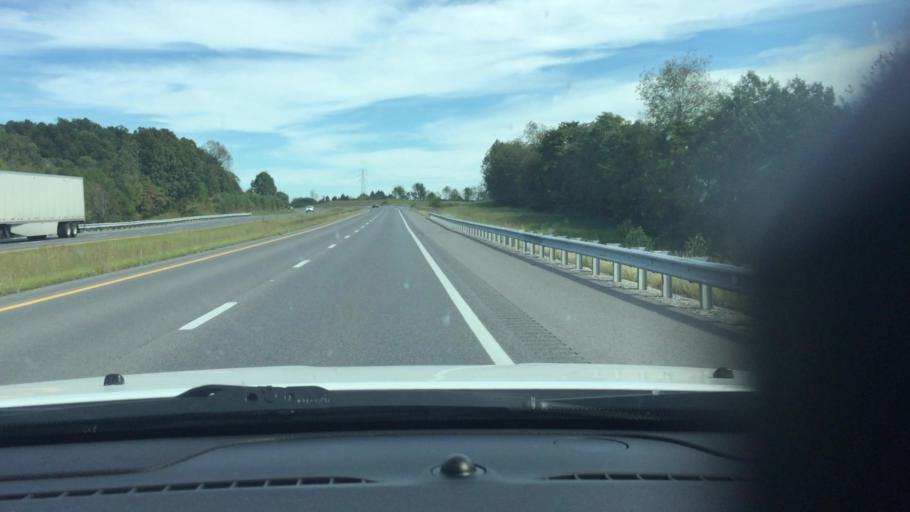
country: US
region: Kentucky
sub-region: Caldwell County
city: Princeton
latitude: 37.1100
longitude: -87.9550
